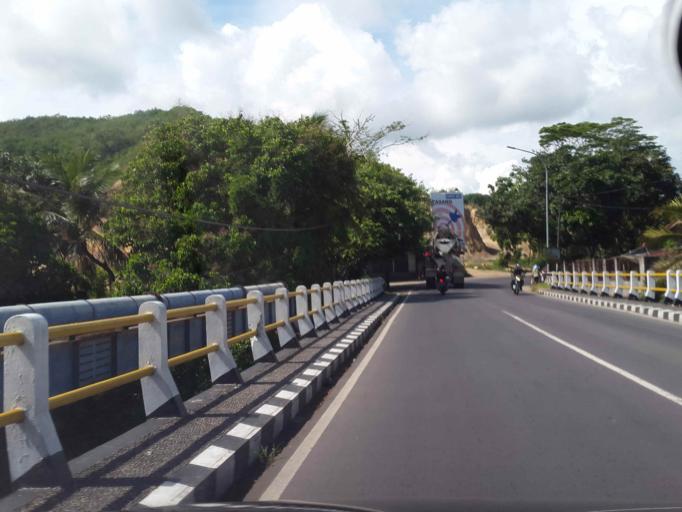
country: ID
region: West Nusa Tenggara
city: Karangkebon Timur
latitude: -8.6908
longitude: 116.1125
